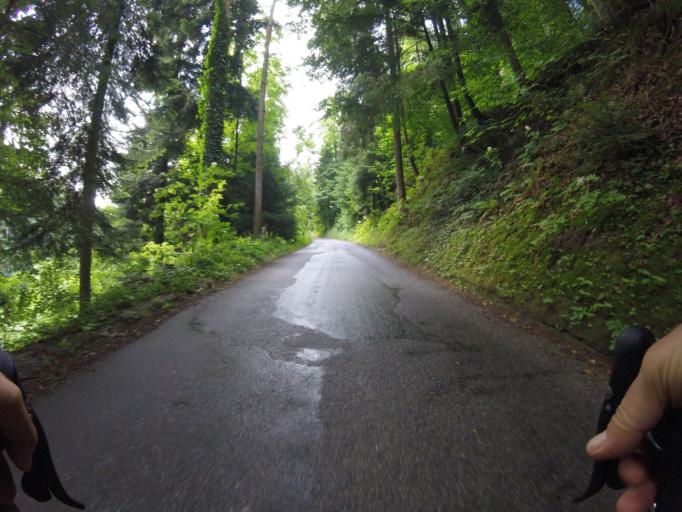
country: CH
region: Bern
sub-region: Emmental District
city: Krauchthal
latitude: 47.0091
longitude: 7.5981
